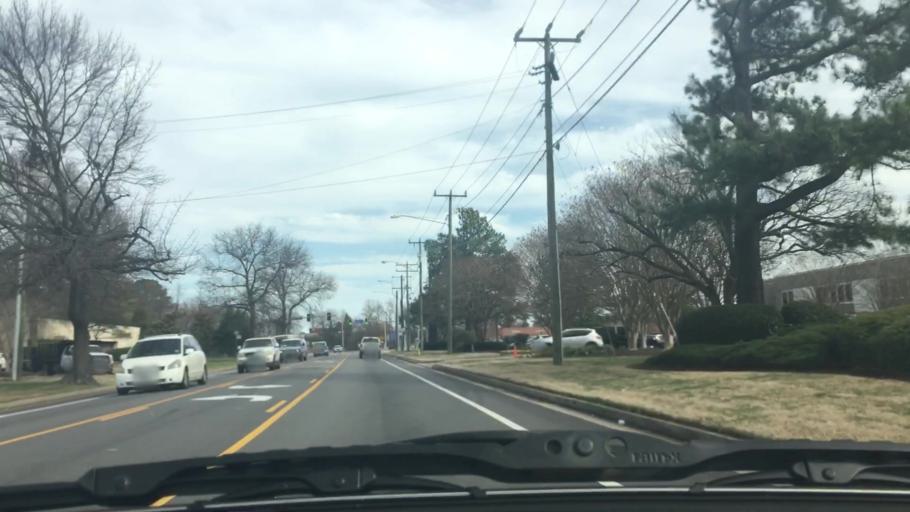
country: US
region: Virginia
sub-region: City of Norfolk
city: Norfolk
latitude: 36.8805
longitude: -76.2192
